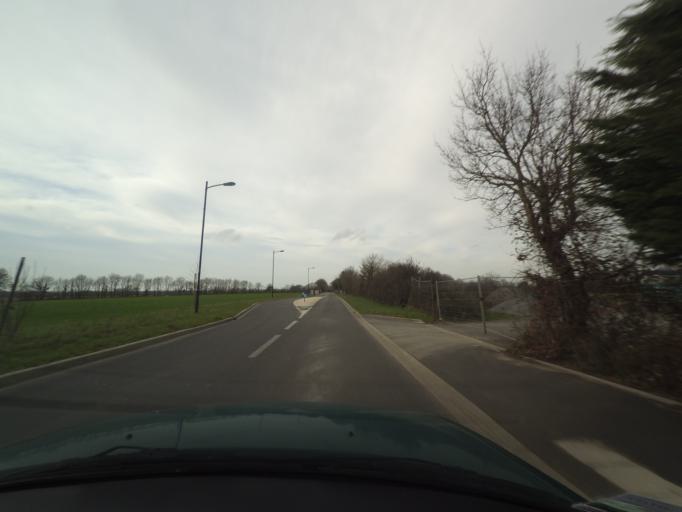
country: FR
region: Pays de la Loire
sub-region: Departement de la Loire-Atlantique
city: Chauve
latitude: 47.1553
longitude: -1.9935
